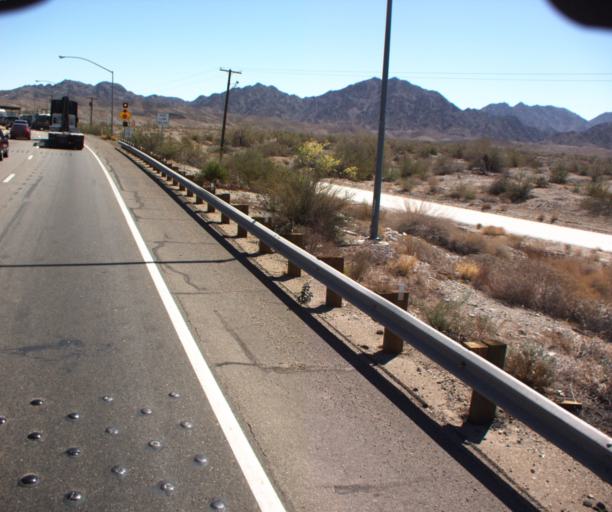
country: US
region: Arizona
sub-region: Yuma County
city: Fortuna Foothills
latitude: 32.6598
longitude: -114.3668
